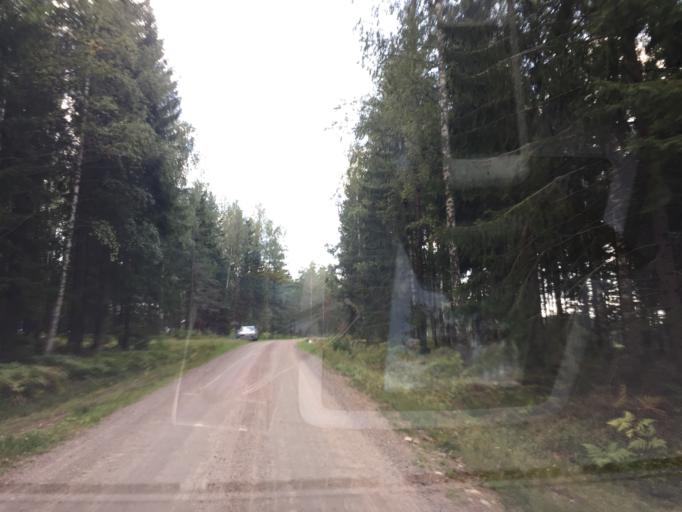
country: SE
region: Soedermanland
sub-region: Vingakers Kommun
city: Vingaker
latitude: 58.9950
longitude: 15.7400
